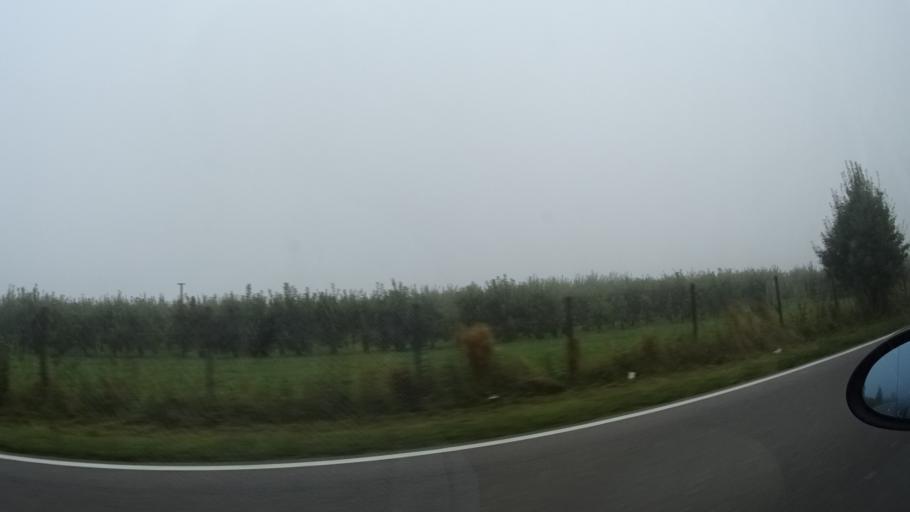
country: DE
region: Baden-Wuerttemberg
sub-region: Karlsruhe Region
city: Olbronn-Durrn
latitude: 48.9780
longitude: 8.7295
